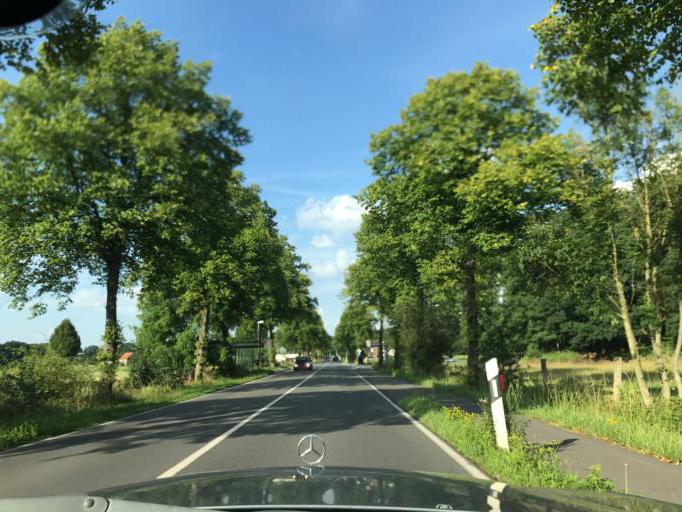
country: DE
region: Lower Saxony
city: Hasbergen
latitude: 52.2154
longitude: 7.9316
